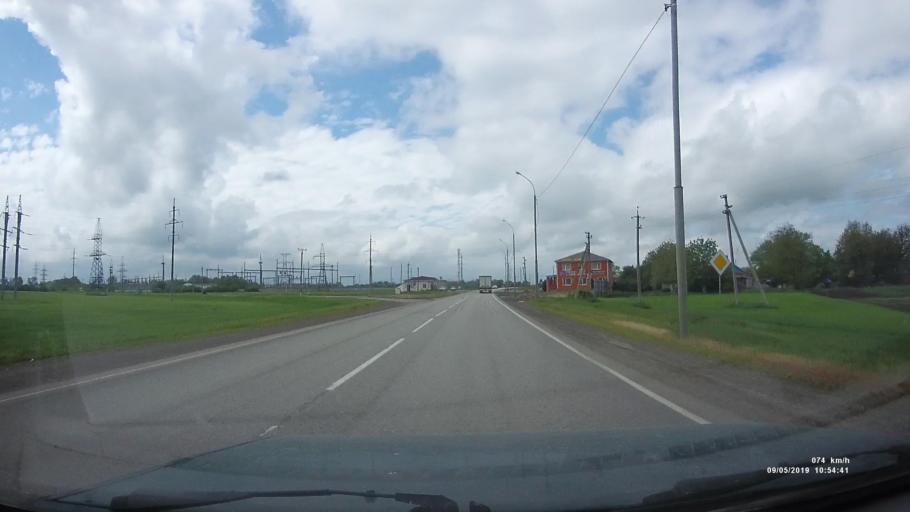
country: RU
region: Rostov
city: Peshkovo
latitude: 46.8760
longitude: 39.3273
